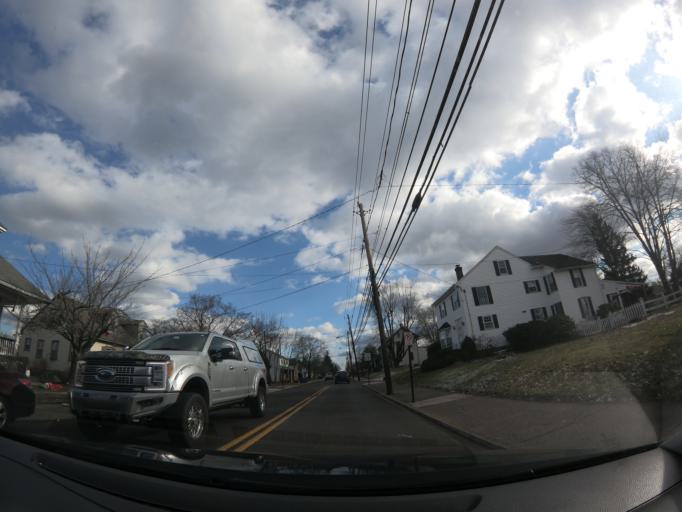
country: US
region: Pennsylvania
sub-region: Montgomery County
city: Telford
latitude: 40.3208
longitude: -75.3210
